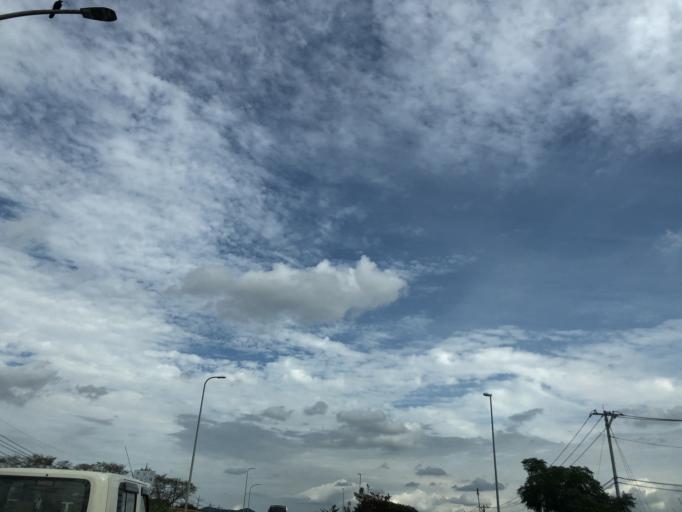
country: JP
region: Tochigi
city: Sano
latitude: 36.2887
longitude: 139.5693
